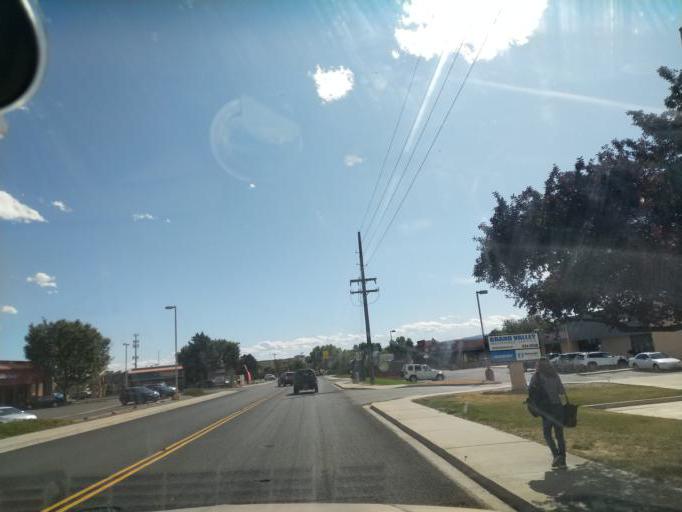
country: US
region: Colorado
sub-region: Mesa County
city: Clifton
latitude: 39.0898
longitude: -108.4597
